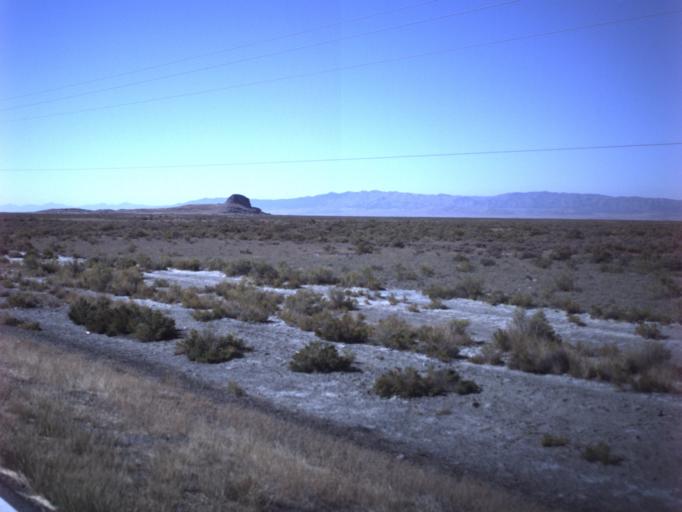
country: US
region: Utah
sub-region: Tooele County
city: Grantsville
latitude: 40.7312
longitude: -112.6573
